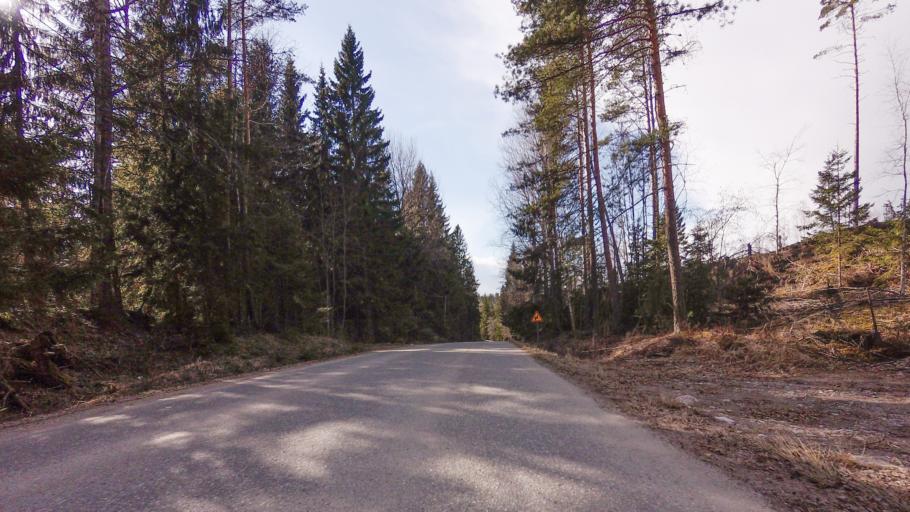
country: FI
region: Varsinais-Suomi
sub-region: Salo
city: Suomusjaervi
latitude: 60.3521
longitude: 23.6578
